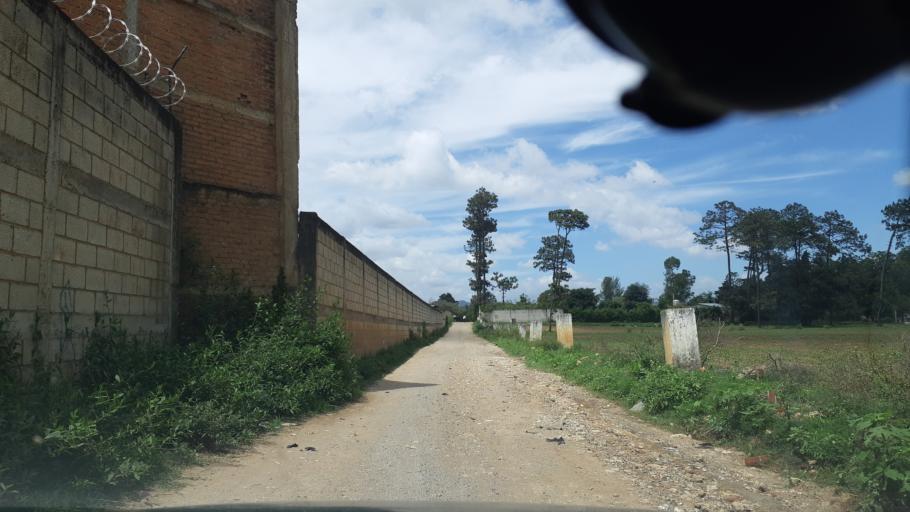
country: GT
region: Chimaltenango
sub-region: Municipio de Chimaltenango
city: Chimaltenango
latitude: 14.6565
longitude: -90.8393
